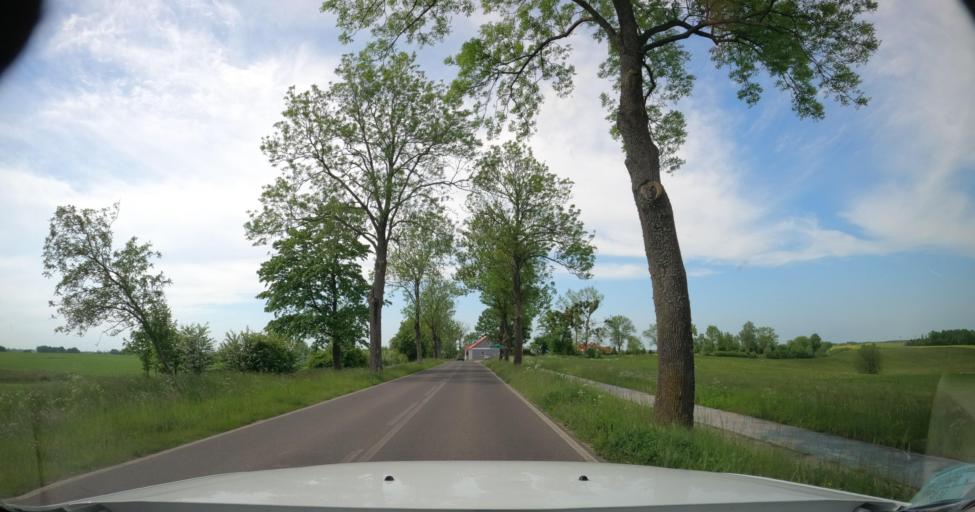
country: PL
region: Warmian-Masurian Voivodeship
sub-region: Powiat lidzbarski
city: Lidzbark Warminski
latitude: 54.1475
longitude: 20.5592
